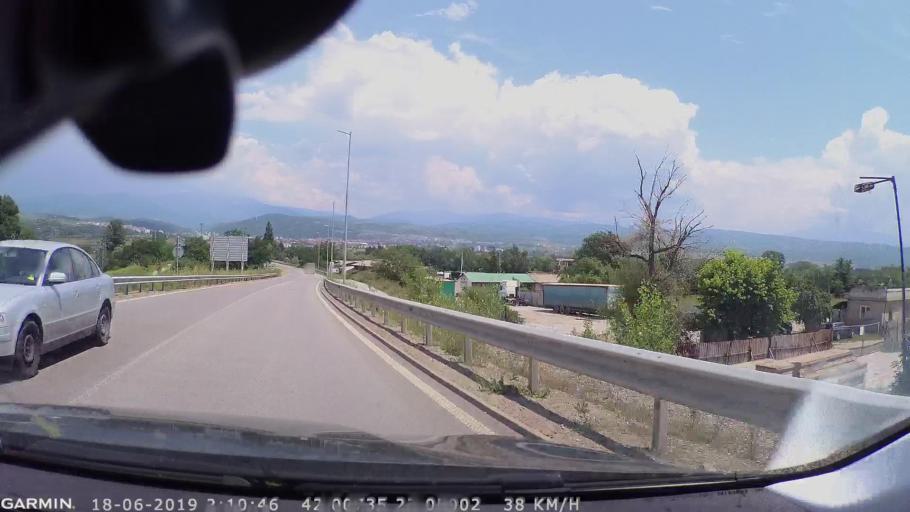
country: BG
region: Blagoevgrad
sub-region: Obshtina Blagoevgrad
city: Blagoevgrad
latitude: 41.9878
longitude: 23.0561
